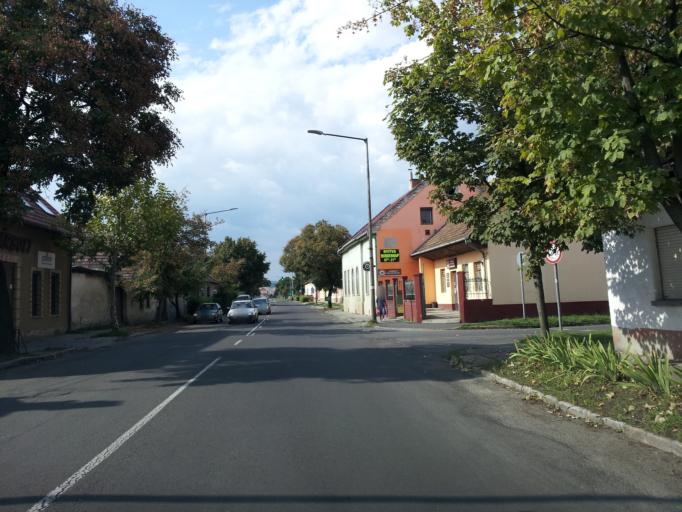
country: HU
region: Pest
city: Vac
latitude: 47.7884
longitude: 19.1193
